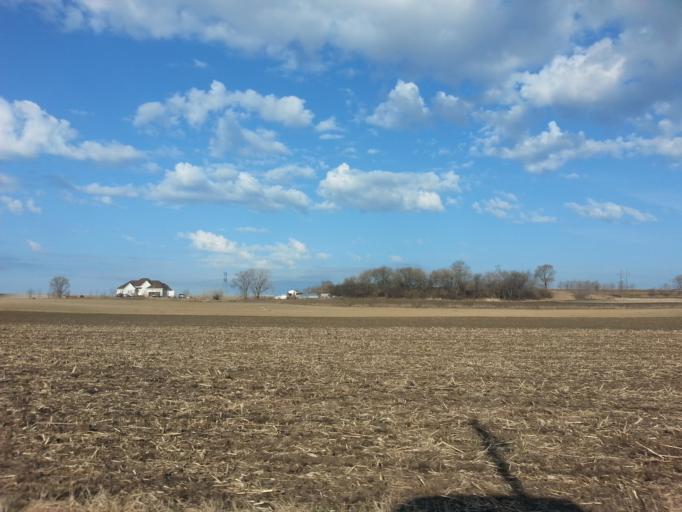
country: US
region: Minnesota
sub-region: Washington County
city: Afton
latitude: 44.8816
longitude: -92.8428
